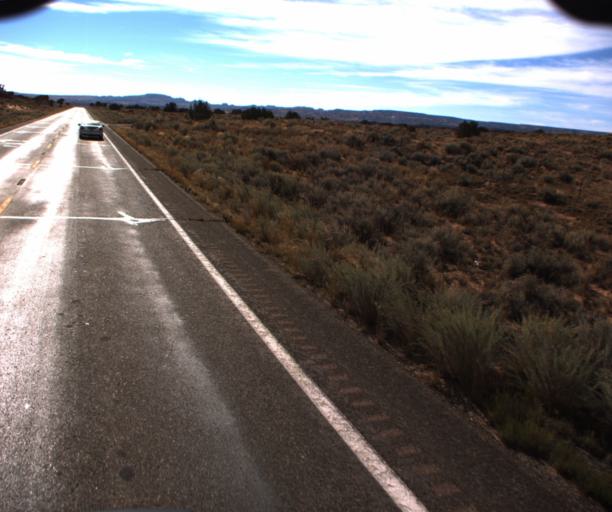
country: US
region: Arizona
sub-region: Coconino County
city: Kaibito
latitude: 36.6348
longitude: -111.2117
